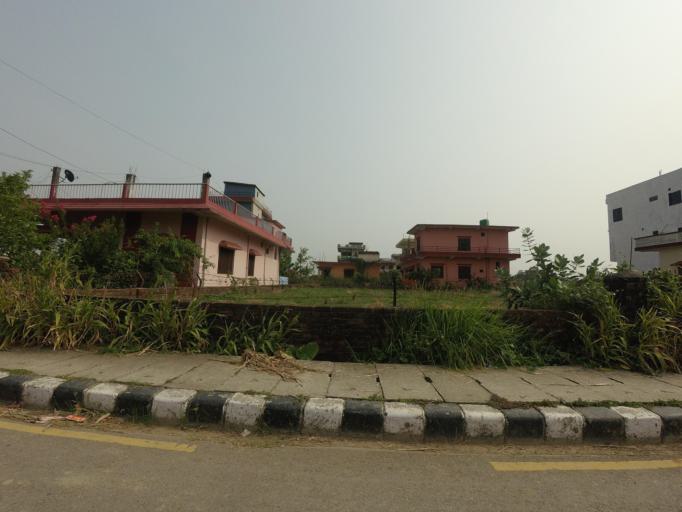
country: NP
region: Western Region
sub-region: Lumbini Zone
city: Bhairahawa
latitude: 27.5176
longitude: 83.4630
